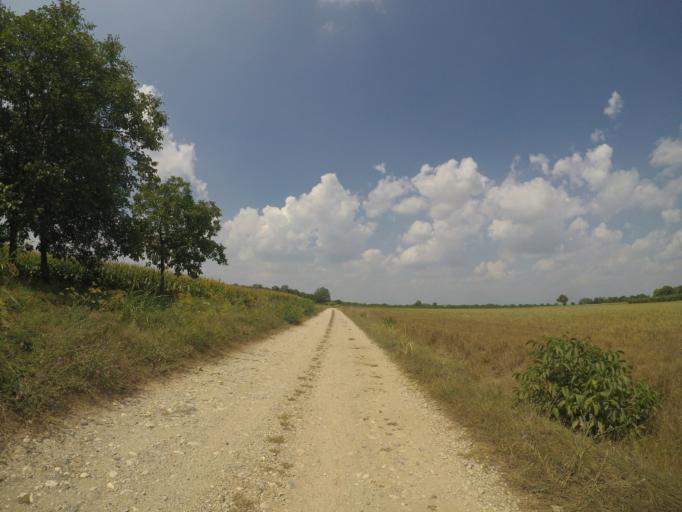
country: IT
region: Friuli Venezia Giulia
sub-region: Provincia di Udine
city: Bertiolo
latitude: 45.9506
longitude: 13.0366
